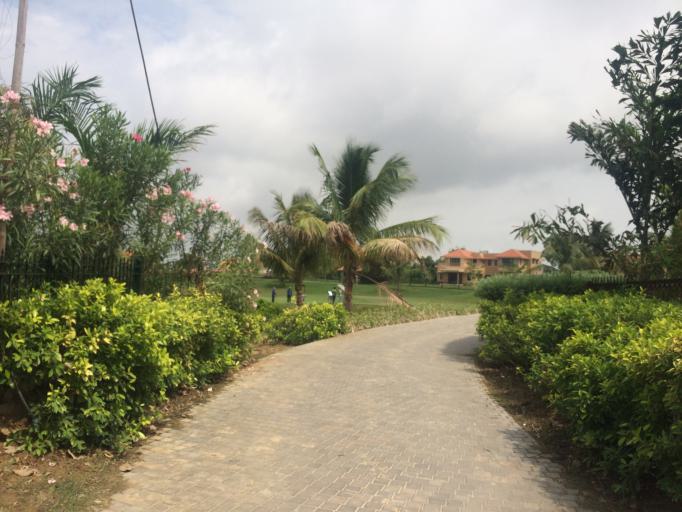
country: IN
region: Gujarat
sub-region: Ahmadabad
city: Sanand
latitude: 23.0220
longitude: 72.3600
